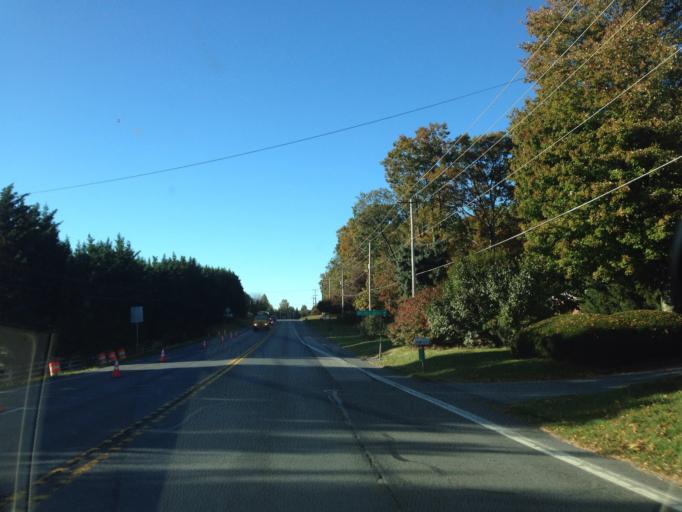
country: US
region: Maryland
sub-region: Carroll County
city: Mount Airy
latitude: 39.4083
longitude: -77.1289
